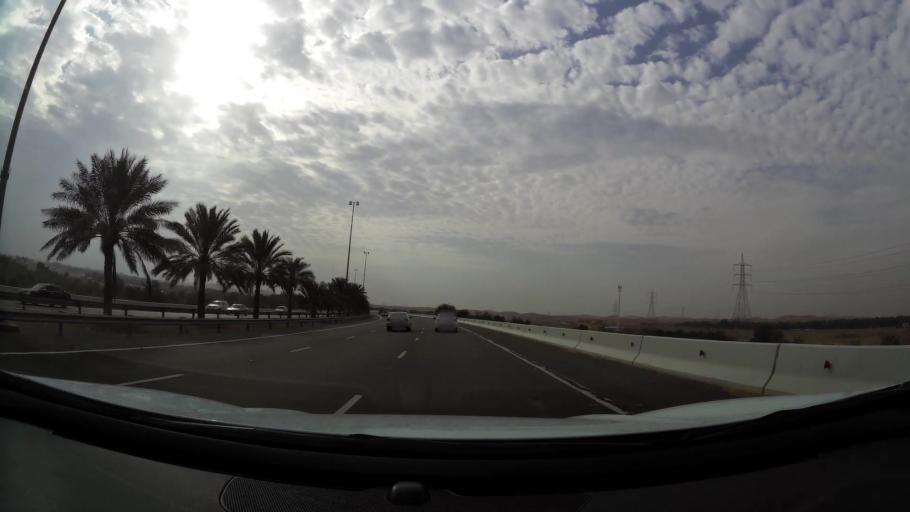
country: AE
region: Abu Dhabi
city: Al Ain
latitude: 24.2056
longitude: 55.5652
